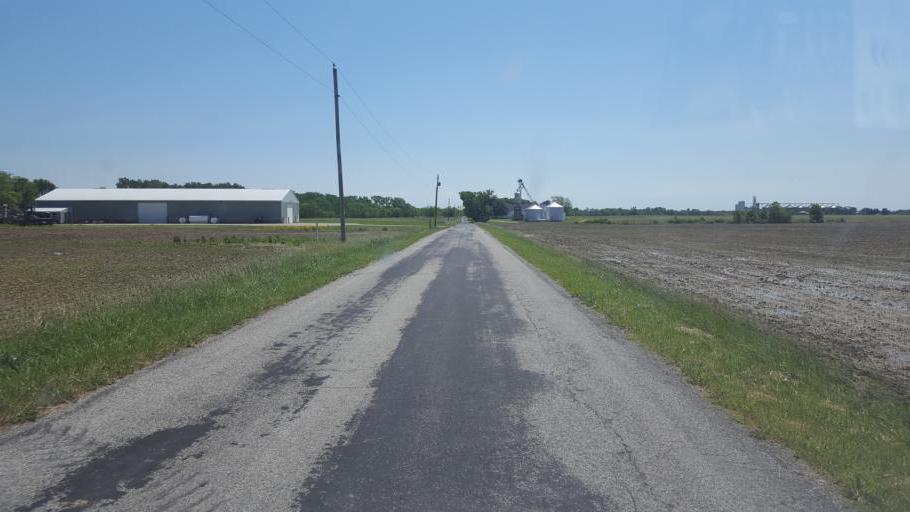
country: US
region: Ohio
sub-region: Hardin County
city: Forest
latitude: 40.6508
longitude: -83.4116
